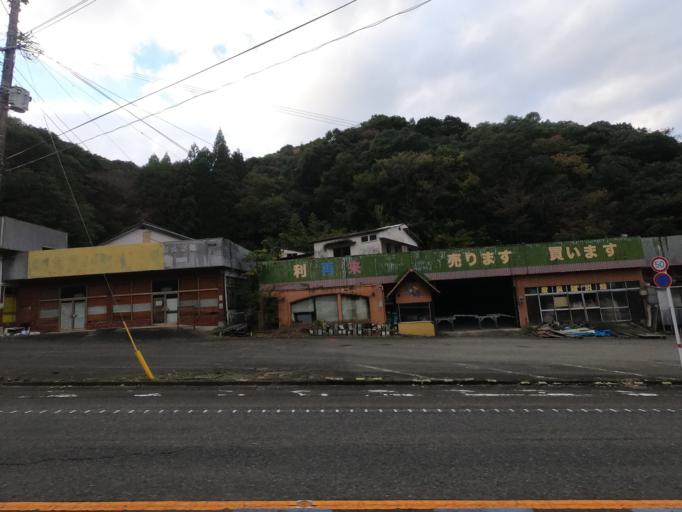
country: JP
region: Kumamoto
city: Minamata
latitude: 32.2478
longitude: 130.5001
